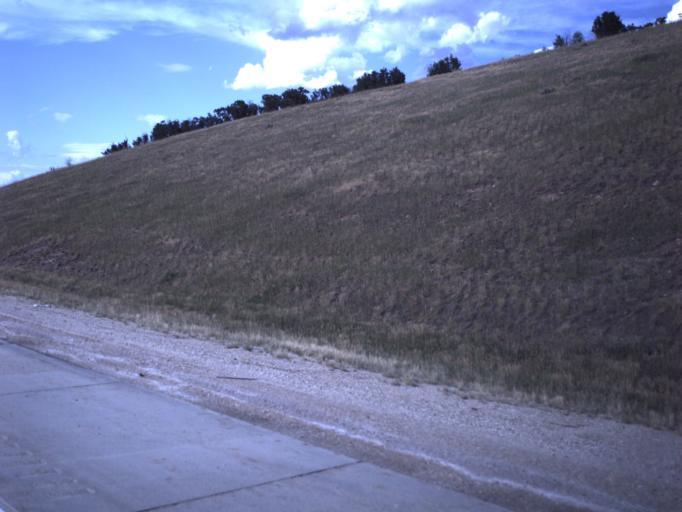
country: US
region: Utah
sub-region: Summit County
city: Park City
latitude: 40.6538
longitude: -111.4567
